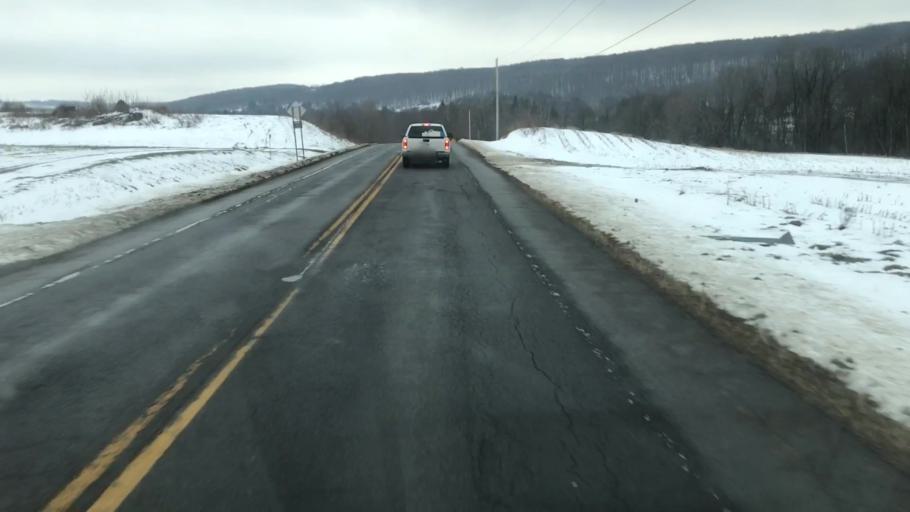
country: US
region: New York
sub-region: Tompkins County
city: Groton
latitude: 42.6852
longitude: -76.3012
